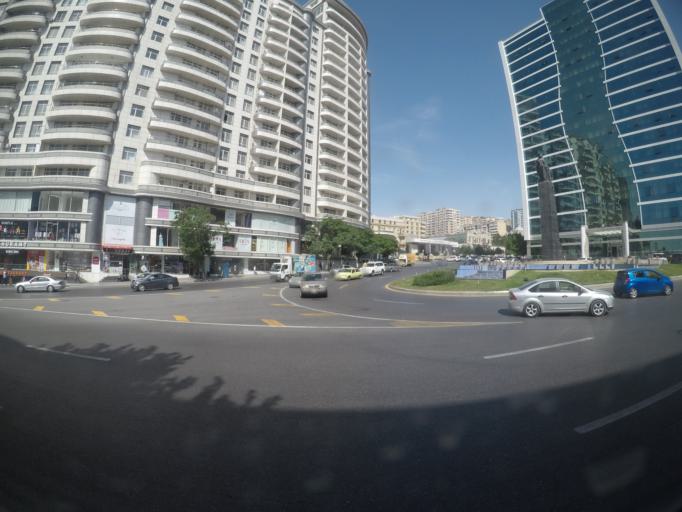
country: AZ
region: Baki
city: Badamdar
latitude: 40.3785
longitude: 49.8314
